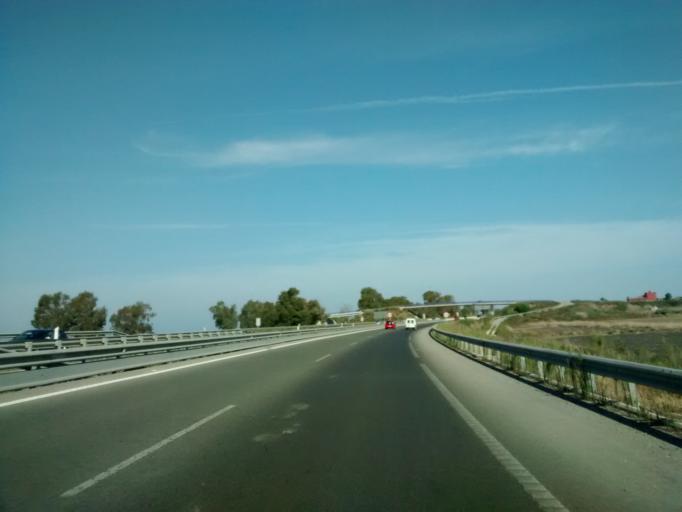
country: ES
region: Andalusia
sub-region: Provincia de Cadiz
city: Chiclana de la Frontera
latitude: 36.3586
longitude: -6.1077
